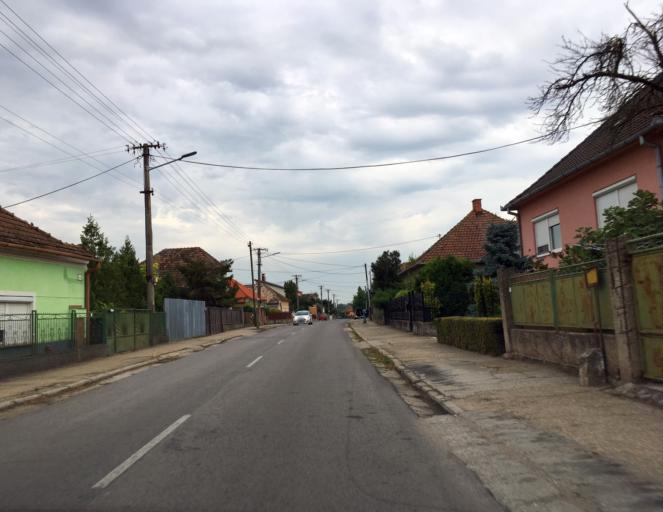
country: SK
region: Trnavsky
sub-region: Okres Dunajska Streda
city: Velky Meder
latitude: 47.9194
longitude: 17.6936
